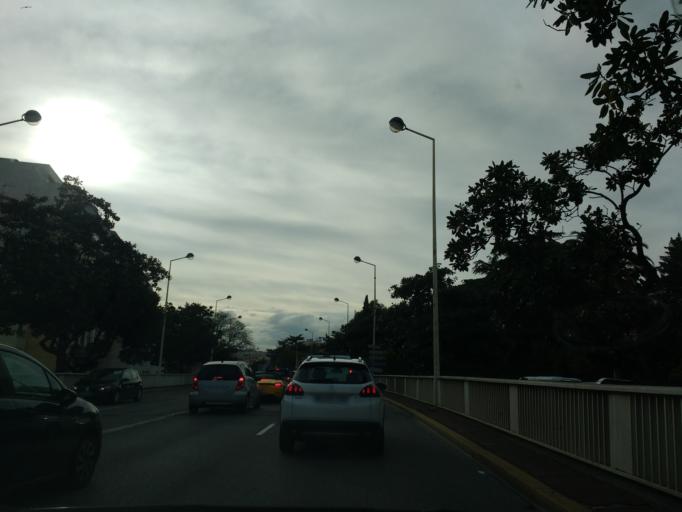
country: FR
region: Provence-Alpes-Cote d'Azur
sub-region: Departement des Alpes-Maritimes
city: Cannes
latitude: 43.5534
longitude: 7.0273
